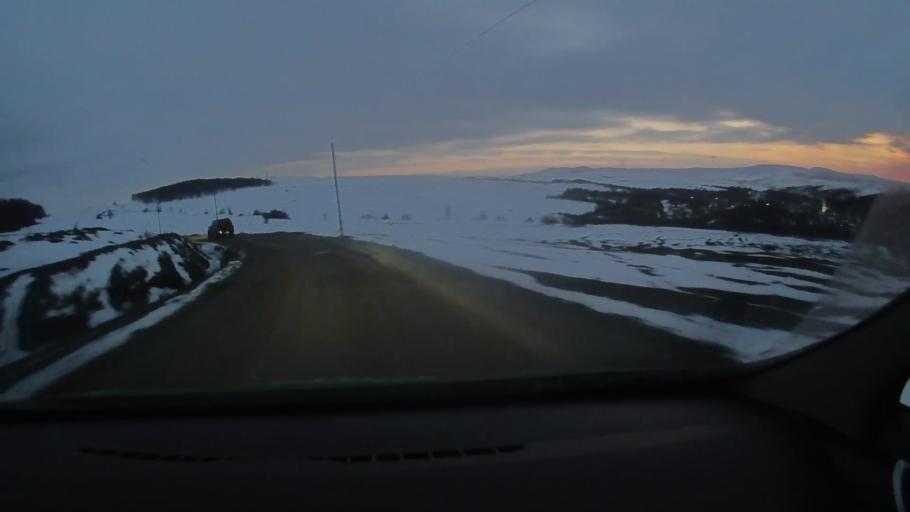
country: RO
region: Harghita
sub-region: Comuna Darjiu
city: Darjiu
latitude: 46.1780
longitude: 25.2472
